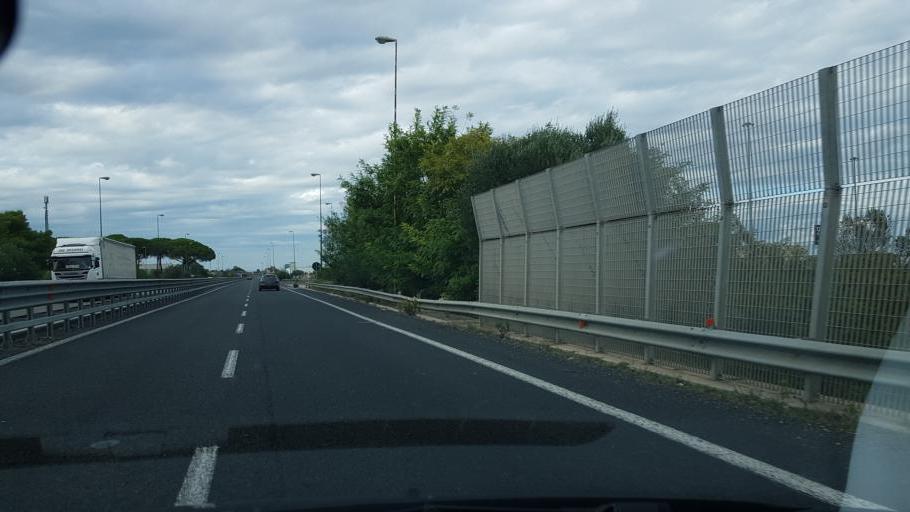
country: IT
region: Apulia
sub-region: Provincia di Lecce
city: Cavallino
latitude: 40.2906
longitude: 18.1977
